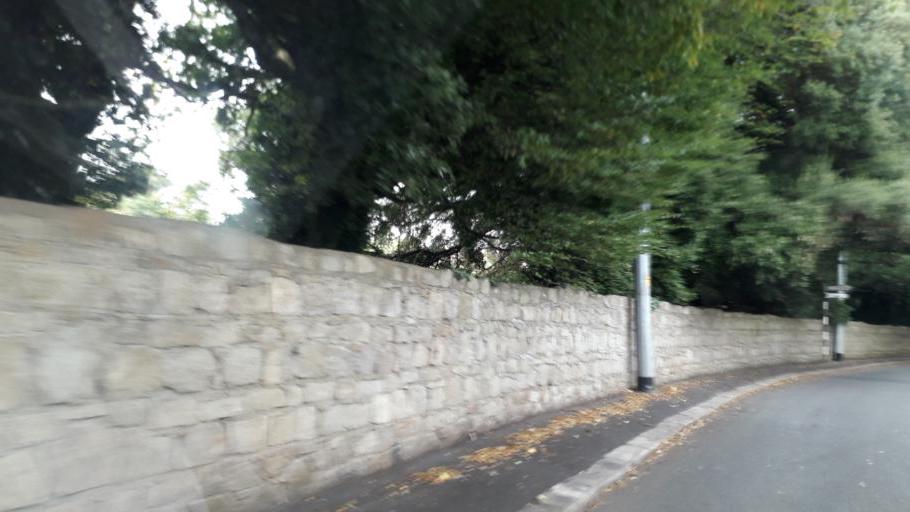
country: IE
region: Leinster
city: Cabinteely
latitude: 53.2551
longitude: -6.1538
